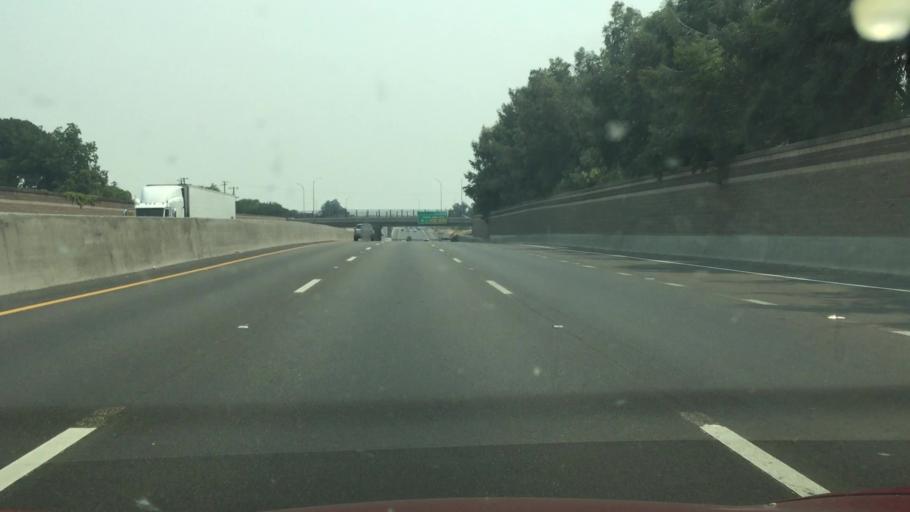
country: US
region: California
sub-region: San Joaquin County
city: Garden Acres
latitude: 37.9563
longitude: -121.2401
